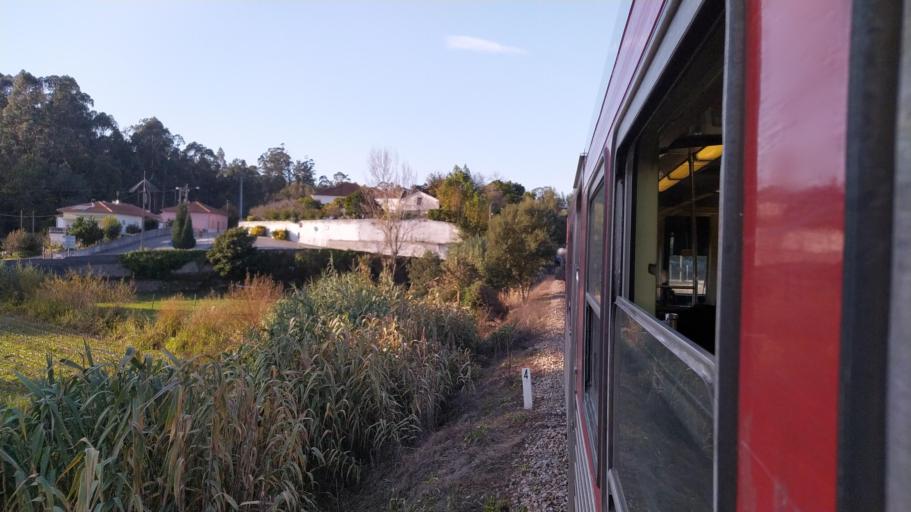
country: PT
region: Aveiro
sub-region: Aveiro
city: Eixo
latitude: 40.6063
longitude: -8.5293
